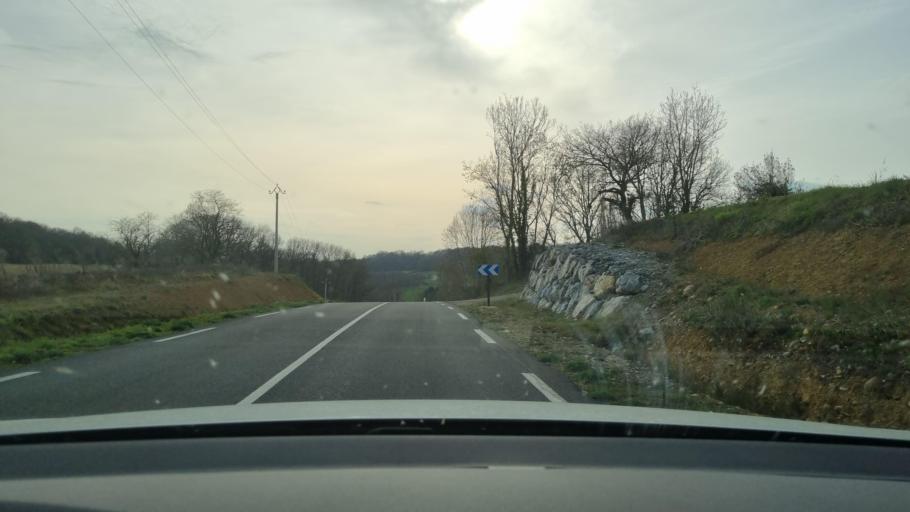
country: FR
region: Aquitaine
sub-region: Departement des Pyrenees-Atlantiques
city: Ger
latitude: 43.3705
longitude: -0.0684
